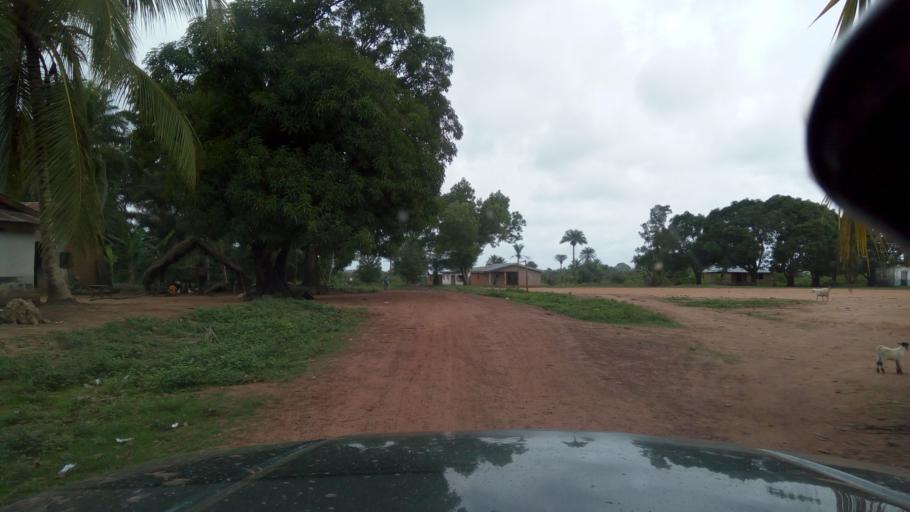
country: SL
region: Northern Province
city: Port Loko
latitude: 8.7661
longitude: -12.9038
